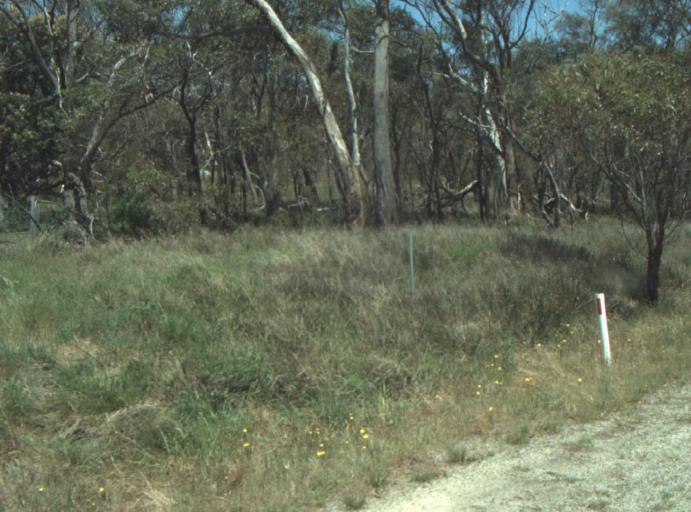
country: AU
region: Victoria
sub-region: Greater Geelong
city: Lara
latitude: -37.8756
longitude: 144.2943
